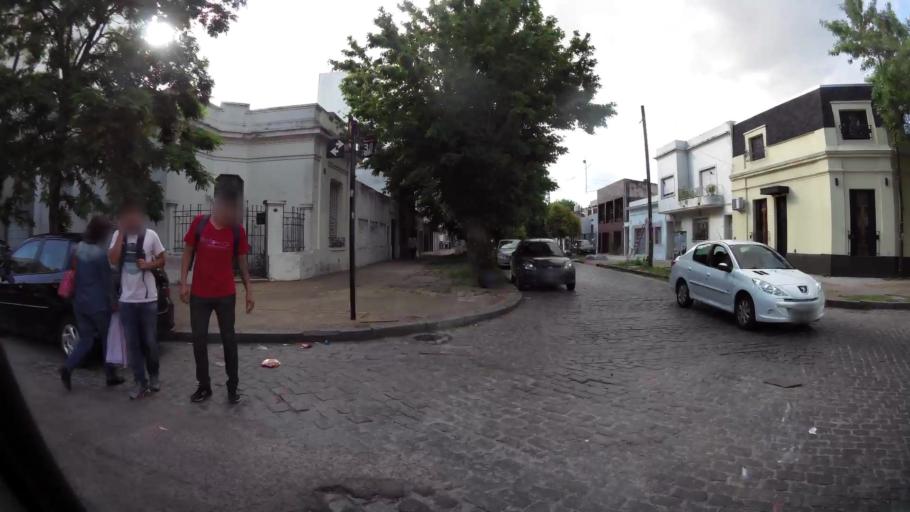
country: AR
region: Buenos Aires
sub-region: Partido de La Plata
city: La Plata
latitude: -34.9019
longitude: -57.9581
